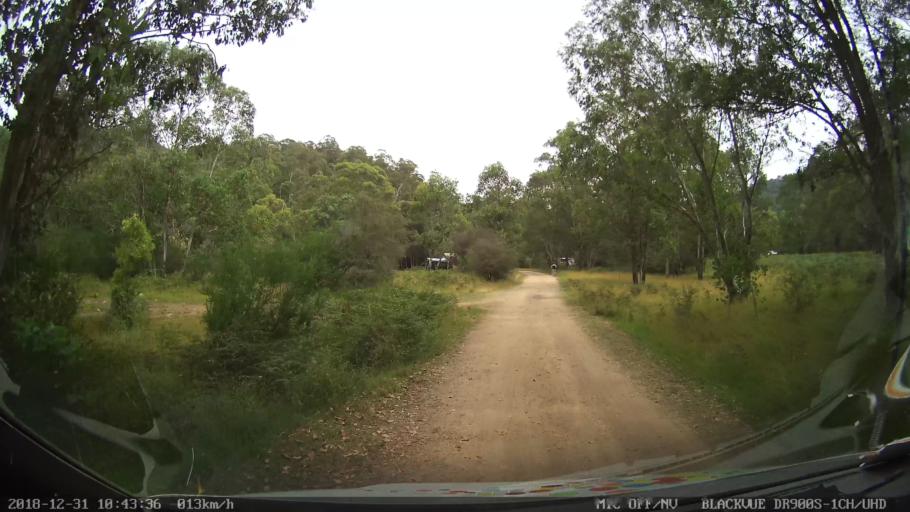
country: AU
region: New South Wales
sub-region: Snowy River
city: Jindabyne
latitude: -36.3802
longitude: 148.1786
